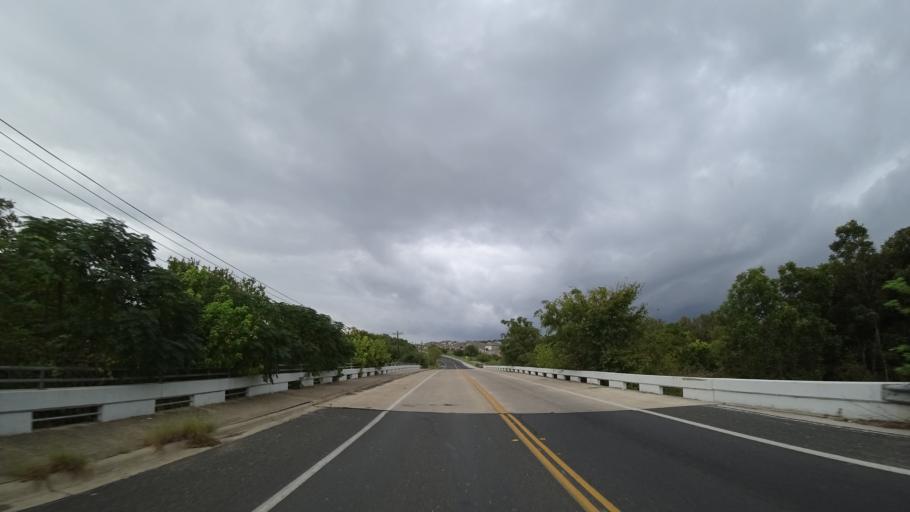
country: US
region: Texas
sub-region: Travis County
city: Onion Creek
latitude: 30.1658
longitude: -97.7348
